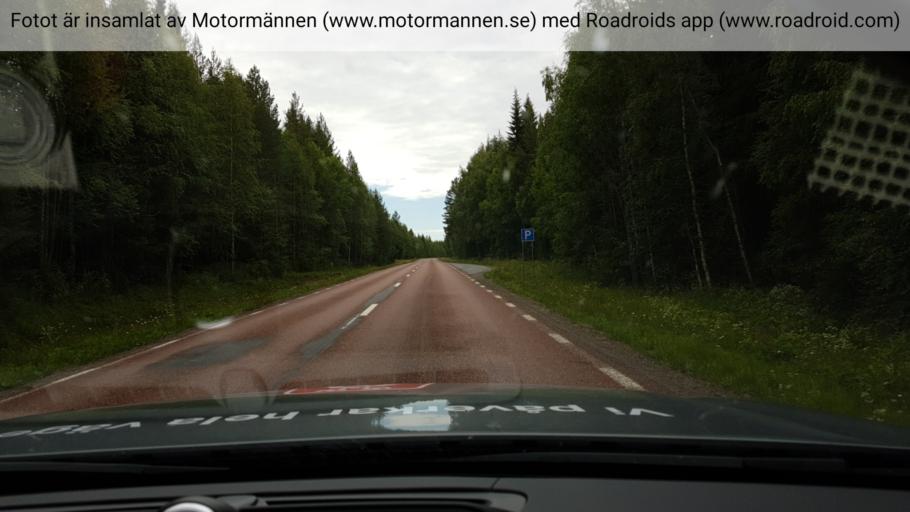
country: SE
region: Vaesterbotten
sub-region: Dorotea Kommun
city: Dorotea
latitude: 64.0847
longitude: 16.0869
